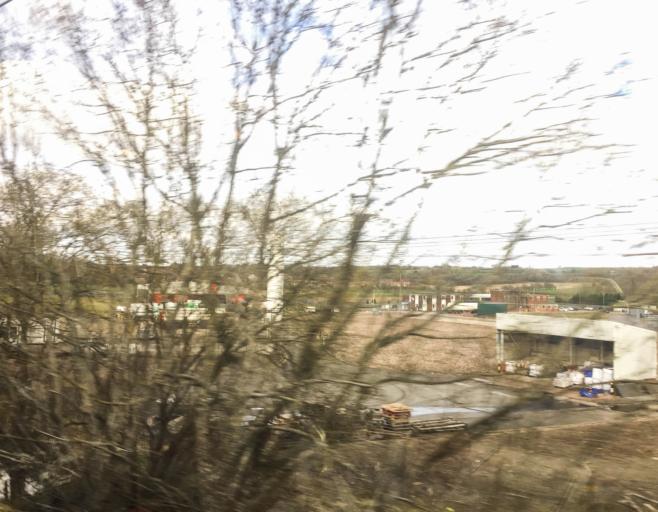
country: GB
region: Scotland
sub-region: North Lanarkshire
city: Newarthill
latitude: 55.8013
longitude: -3.9546
